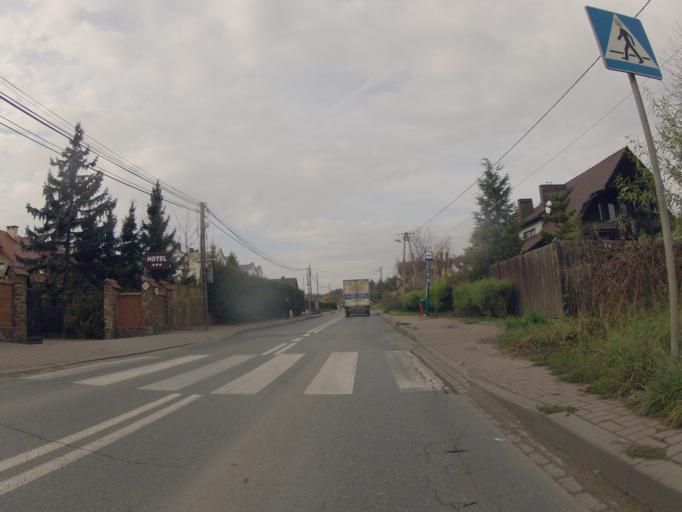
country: PL
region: Lesser Poland Voivodeship
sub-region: Powiat krakowski
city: Rzaska
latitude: 50.0914
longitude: 19.8297
